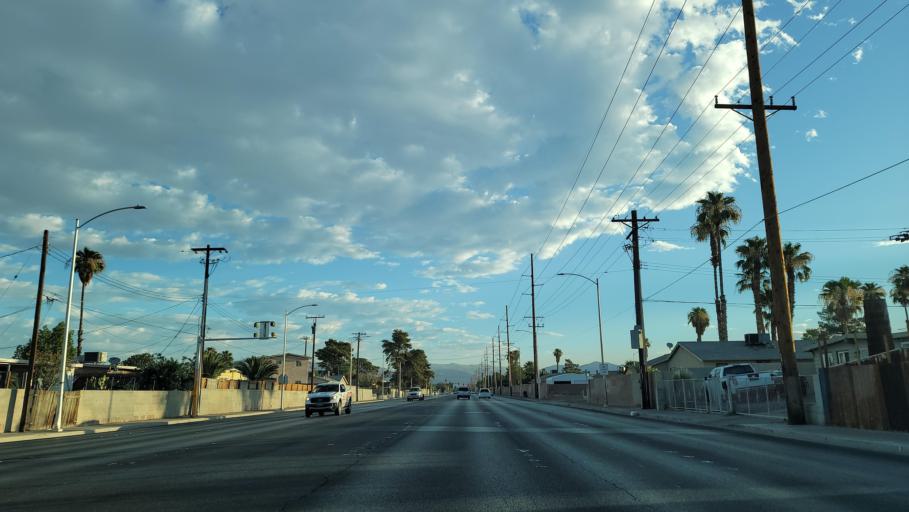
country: US
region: Nevada
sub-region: Clark County
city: North Las Vegas
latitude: 36.1841
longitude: -115.0983
